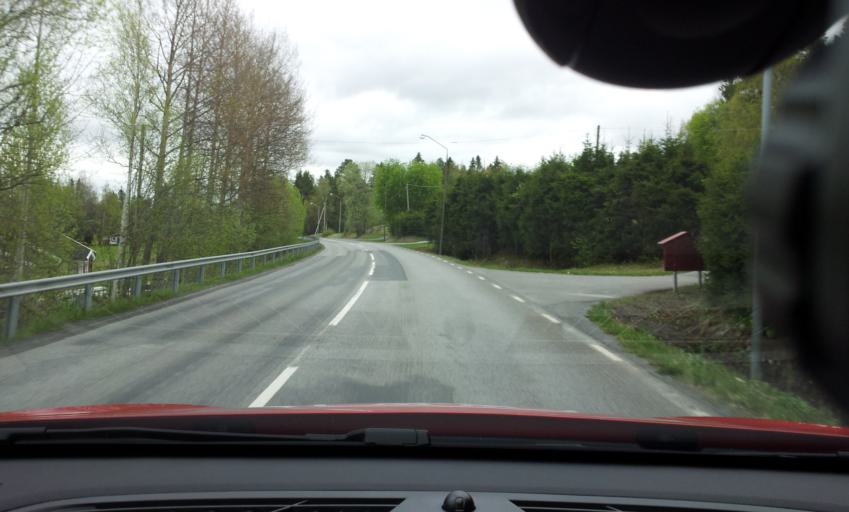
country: SE
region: Jaemtland
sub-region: OEstersunds Kommun
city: Ostersund
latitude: 63.1374
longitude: 14.6335
